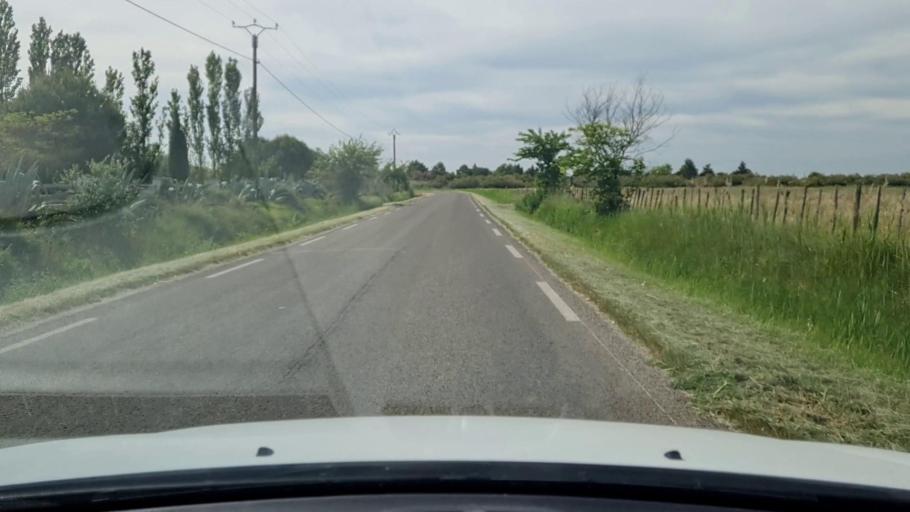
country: FR
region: Languedoc-Roussillon
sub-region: Departement du Gard
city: Aigues-Mortes
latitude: 43.6144
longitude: 4.2075
